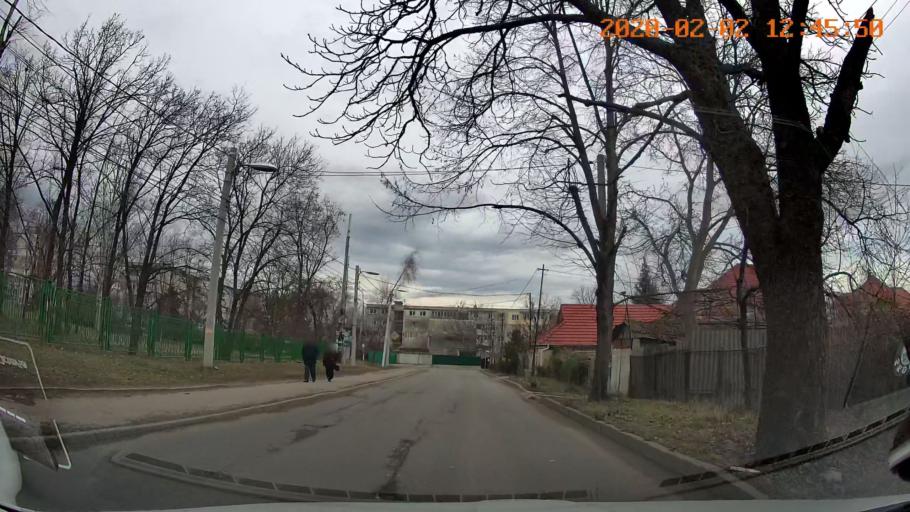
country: MD
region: Chisinau
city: Chisinau
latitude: 47.0069
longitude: 28.8163
